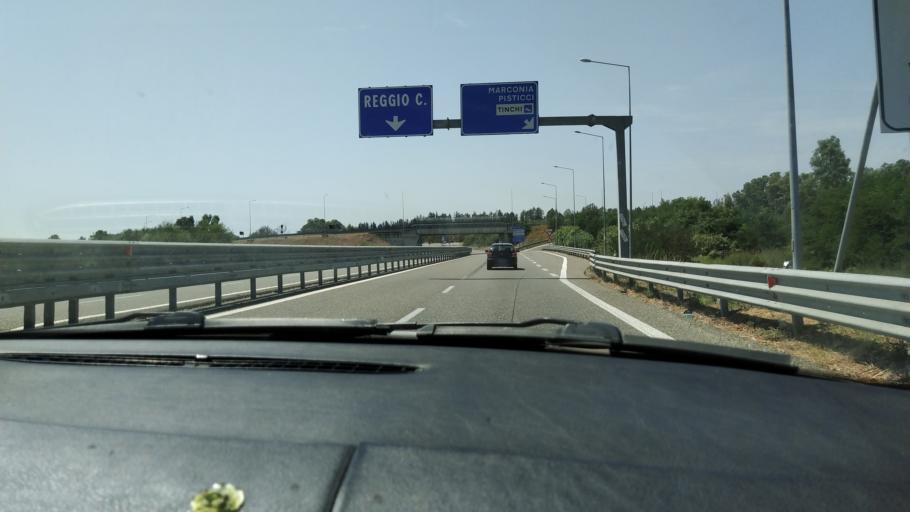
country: IT
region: Basilicate
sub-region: Provincia di Matera
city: Marconia
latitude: 40.3664
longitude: 16.7810
